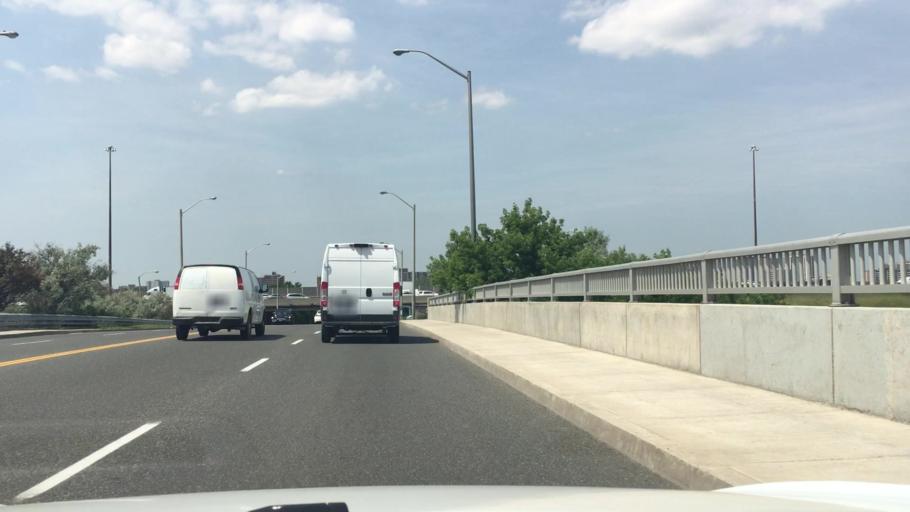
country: CA
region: Ontario
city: Scarborough
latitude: 43.7709
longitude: -79.2935
